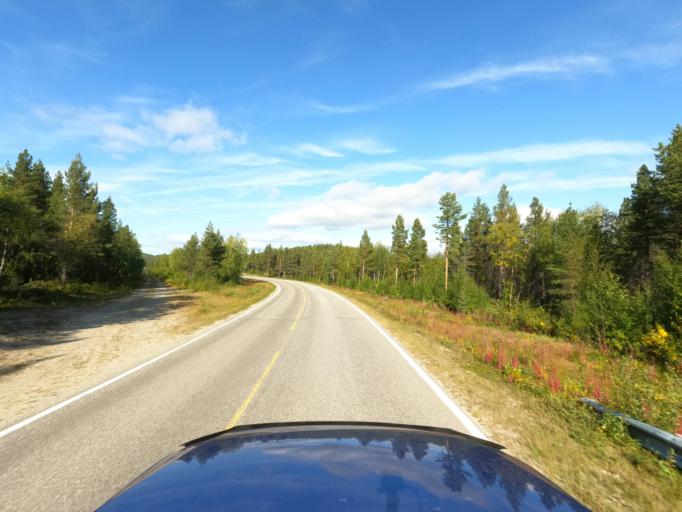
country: NO
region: Finnmark Fylke
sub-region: Porsanger
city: Lakselv
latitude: 69.8205
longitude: 25.1568
